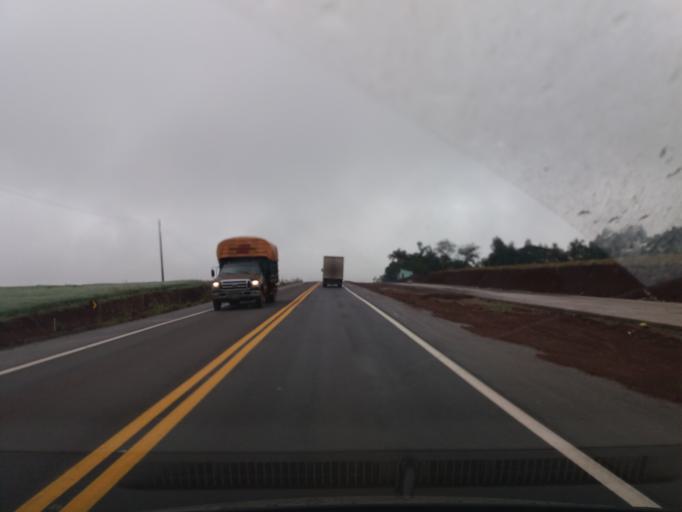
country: BR
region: Parana
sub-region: Realeza
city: Realeza
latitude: -25.4437
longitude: -53.5782
